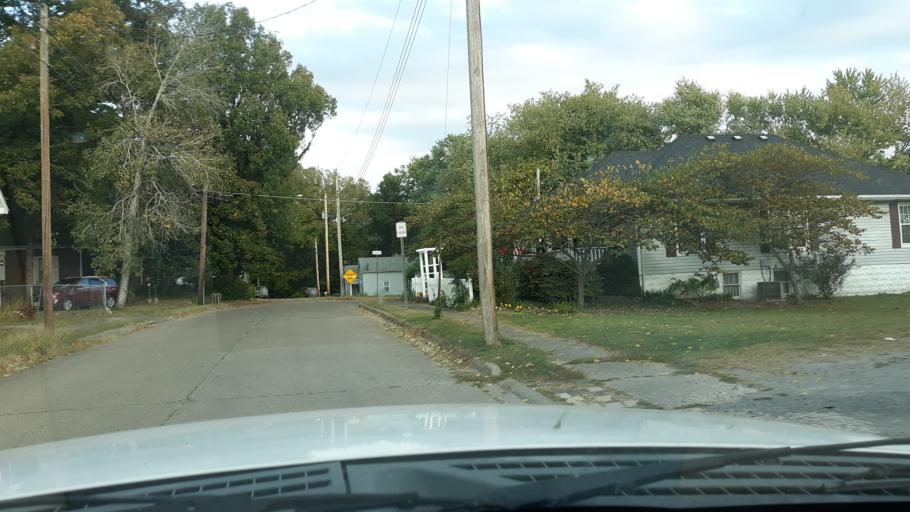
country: US
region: Illinois
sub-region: Saline County
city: Eldorado
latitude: 37.8161
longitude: -88.4343
